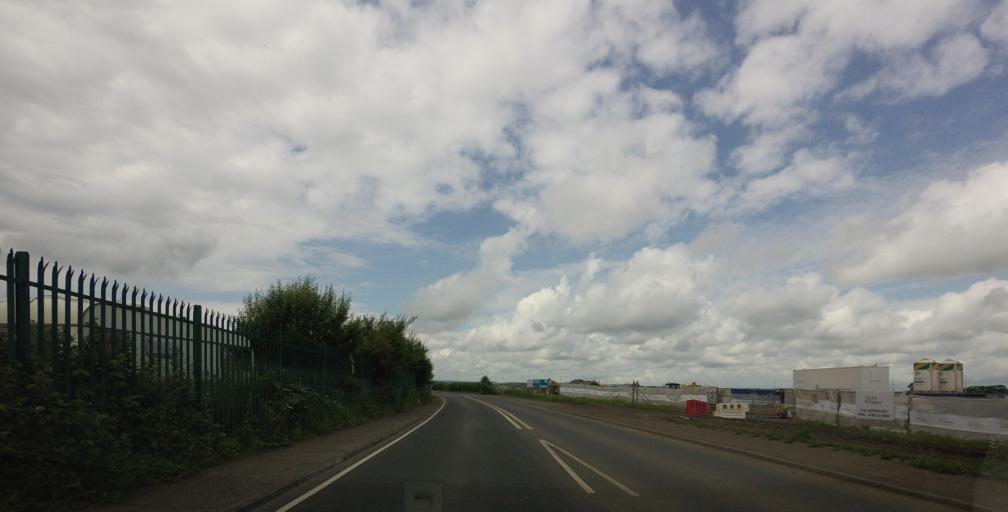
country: GB
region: Scotland
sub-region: West Lothian
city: Kirknewton
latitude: 55.9008
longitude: -3.4322
